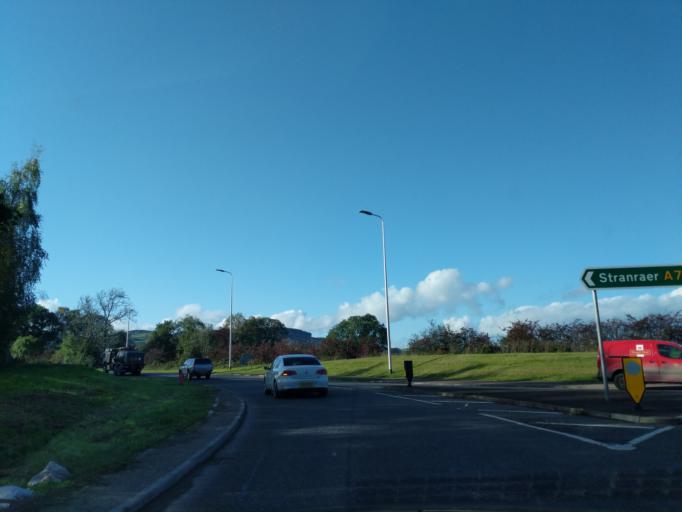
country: GB
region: Scotland
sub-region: Dumfries and Galloway
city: Dumfries
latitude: 55.0611
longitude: -3.6559
